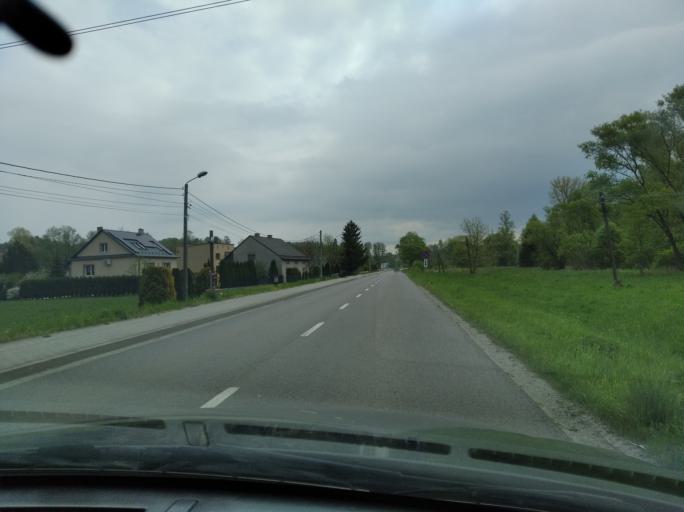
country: PL
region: Lesser Poland Voivodeship
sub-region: Powiat tarnowski
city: Skrzyszow
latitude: 49.9871
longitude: 21.0879
